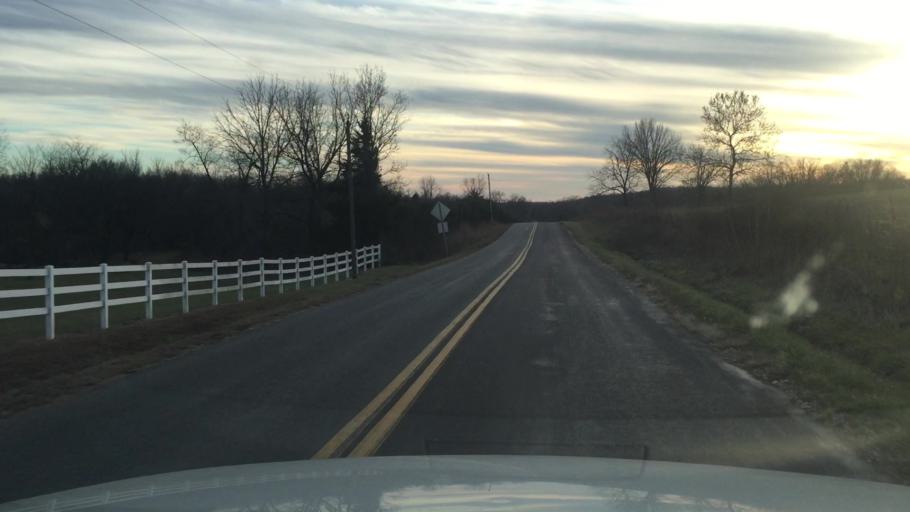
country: US
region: Missouri
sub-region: Miller County
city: Eldon
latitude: 38.3690
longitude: -92.6806
